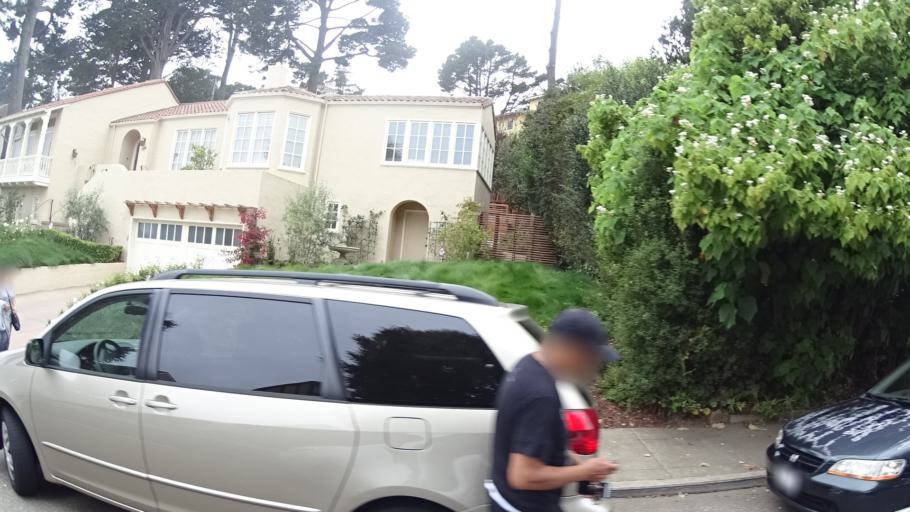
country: US
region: California
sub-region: San Mateo County
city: Daly City
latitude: 37.7318
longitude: -122.4585
